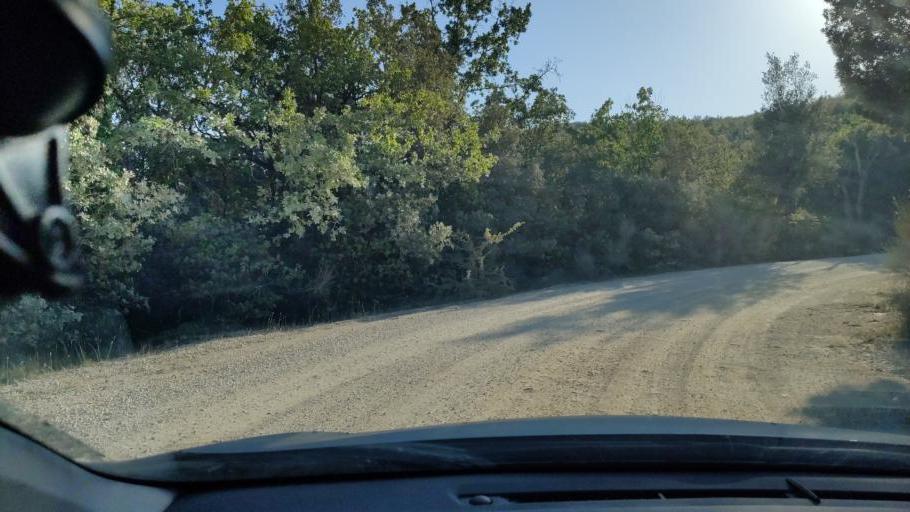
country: IT
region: Umbria
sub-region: Provincia di Terni
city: Amelia
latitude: 42.5349
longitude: 12.3803
